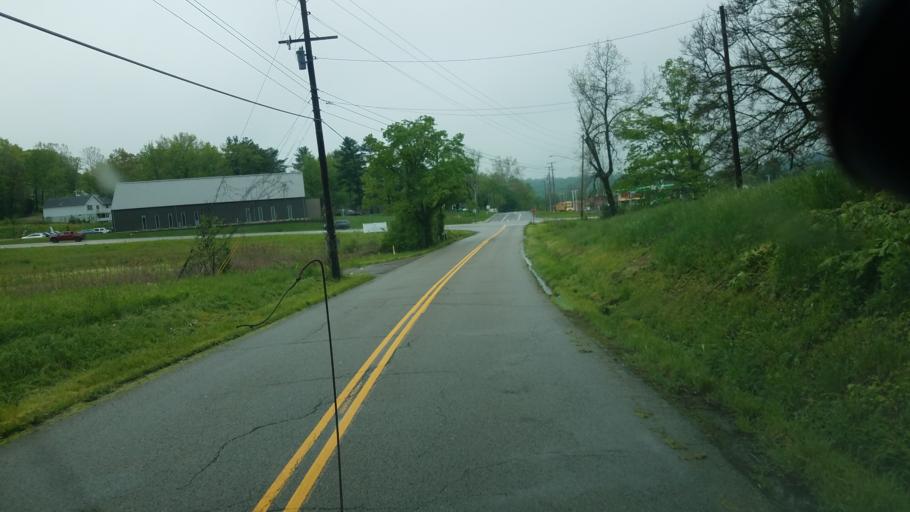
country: US
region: Ohio
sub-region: Muskingum County
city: North Zanesville
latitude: 39.9790
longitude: -82.0516
